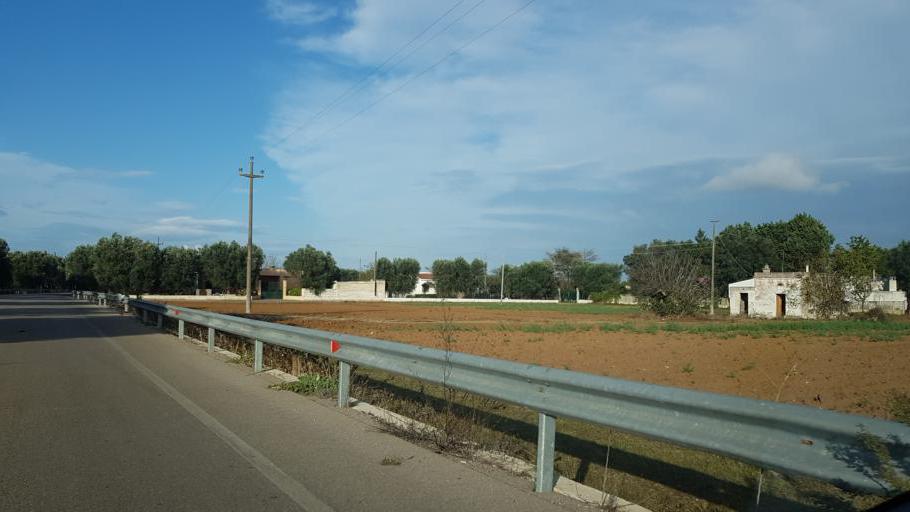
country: IT
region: Apulia
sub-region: Provincia di Brindisi
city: Oria
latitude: 40.5255
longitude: 17.6538
